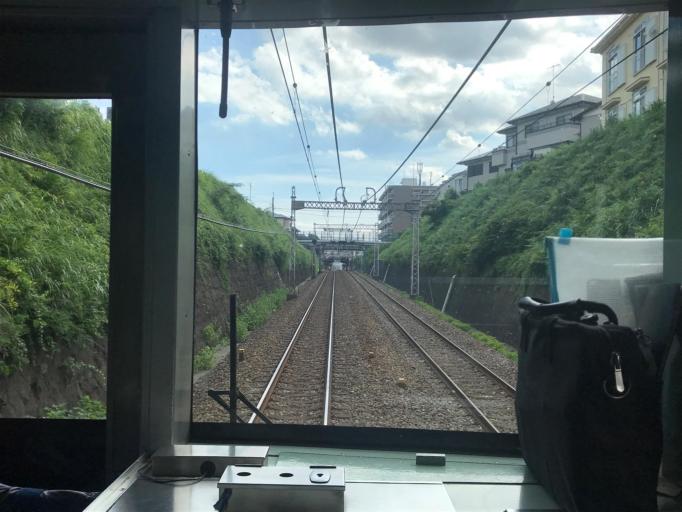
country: JP
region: Kanagawa
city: Atsugi
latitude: 35.4164
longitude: 139.3404
